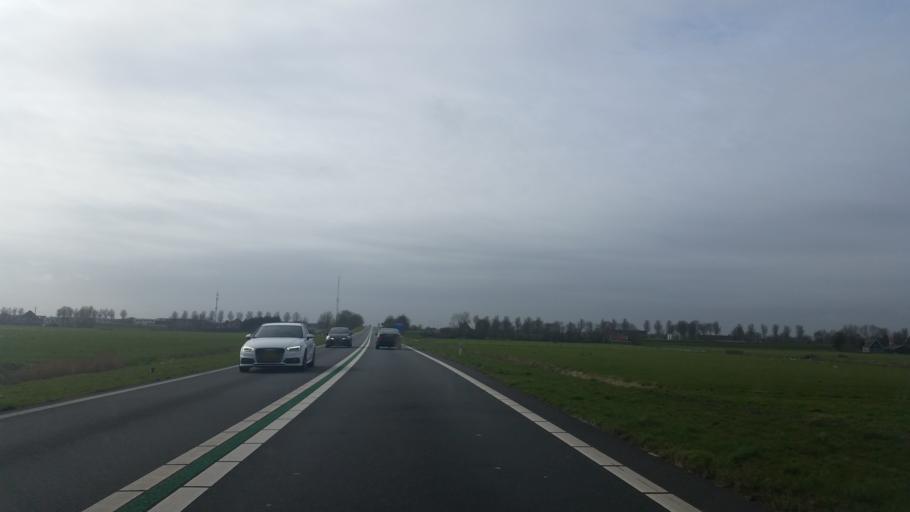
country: NL
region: North Holland
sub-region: Gemeente Beemster
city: Halfweg
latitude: 52.5511
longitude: 4.8587
